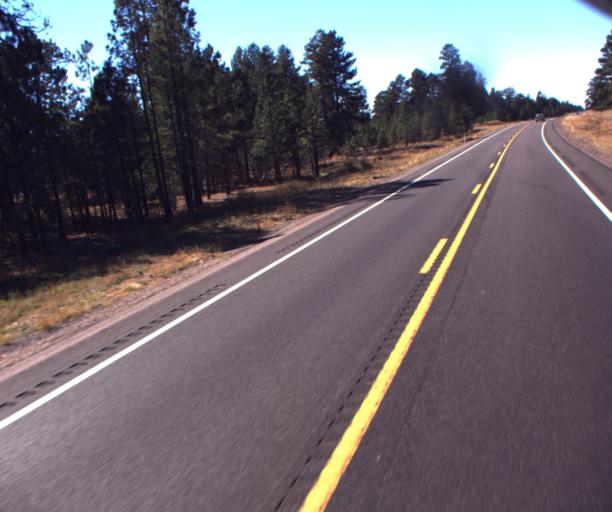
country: US
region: Arizona
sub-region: Apache County
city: Saint Michaels
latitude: 35.6858
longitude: -109.2394
